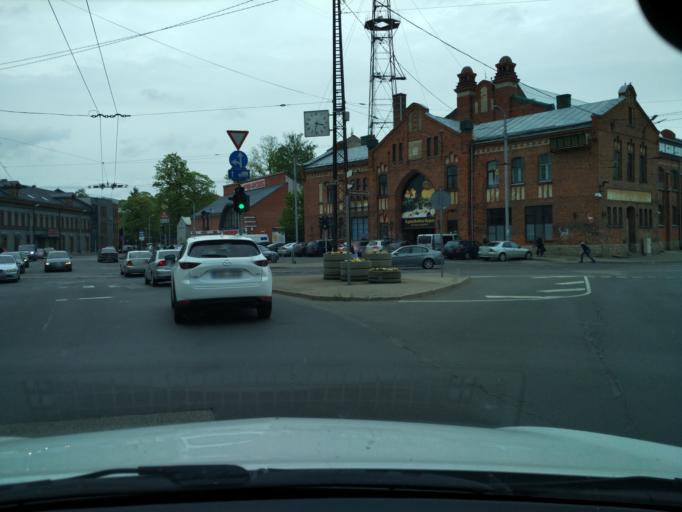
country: LV
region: Marupe
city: Marupe
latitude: 56.9352
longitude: 24.0712
